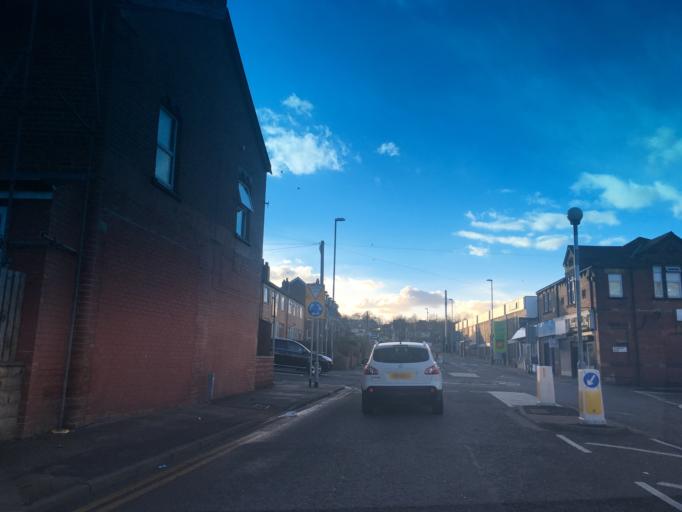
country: GB
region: England
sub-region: City and Borough of Leeds
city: Leeds
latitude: 53.7889
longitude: -1.5839
